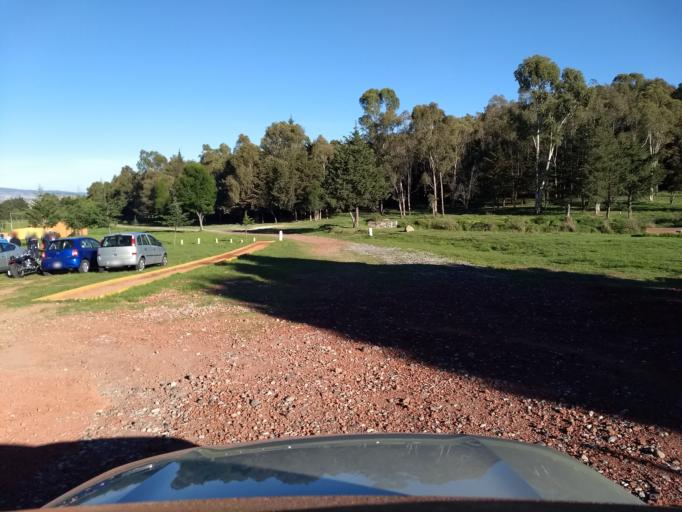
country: MX
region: Mexico
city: San Marcos Yachihuacaltepec
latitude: 19.3117
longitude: -99.6859
